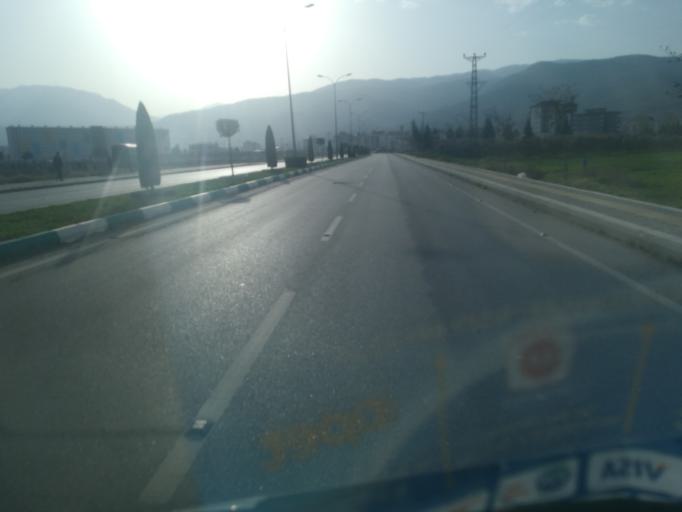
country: TR
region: Osmaniye
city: Osmaniye
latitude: 37.0518
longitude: 36.2253
